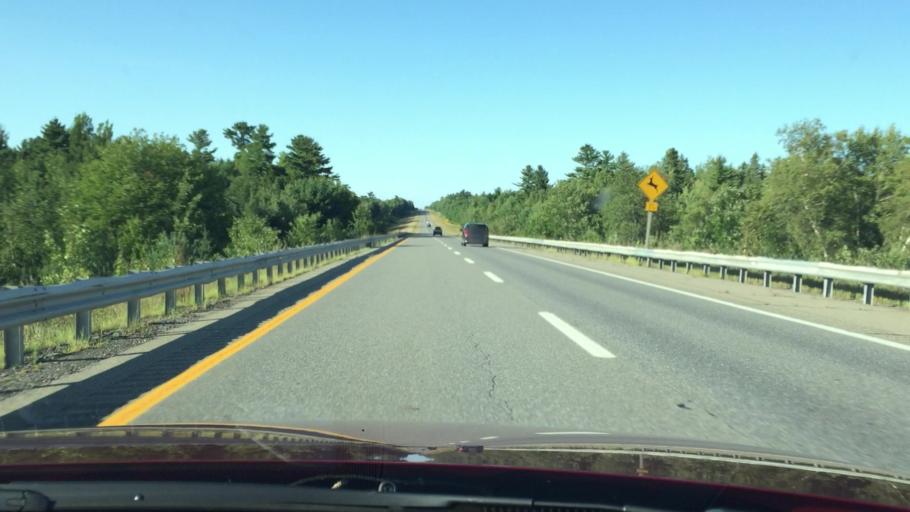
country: US
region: Maine
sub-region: Penobscot County
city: Lincoln
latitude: 45.3966
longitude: -68.6000
